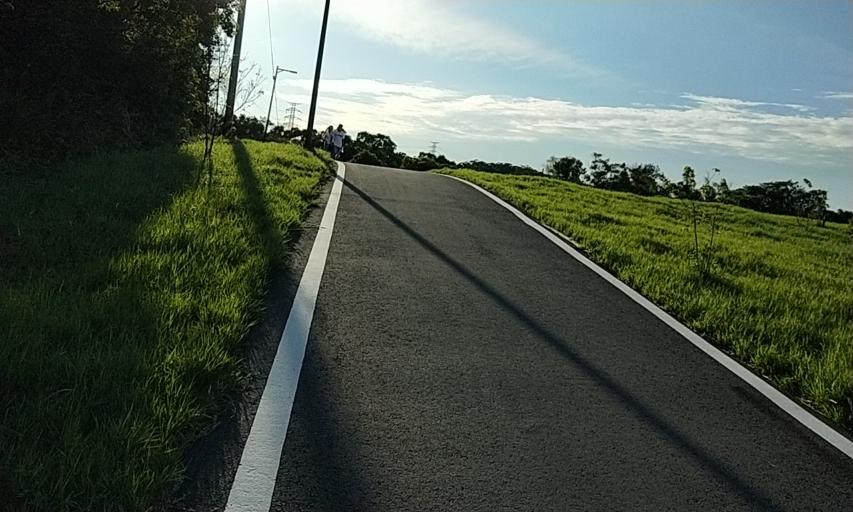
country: TW
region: Taiwan
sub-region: Hsinchu
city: Hsinchu
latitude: 24.7673
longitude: 120.9356
